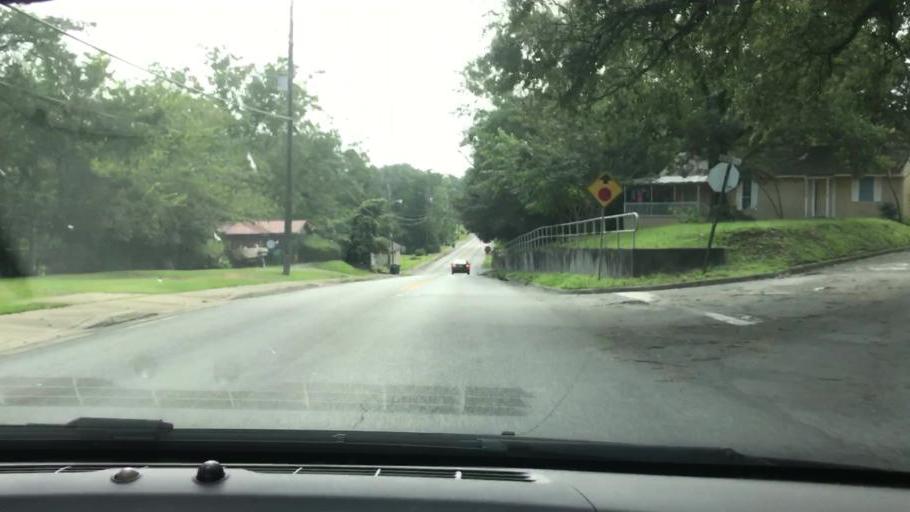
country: US
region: Florida
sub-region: Jackson County
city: Marianna
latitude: 30.7689
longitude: -85.2304
